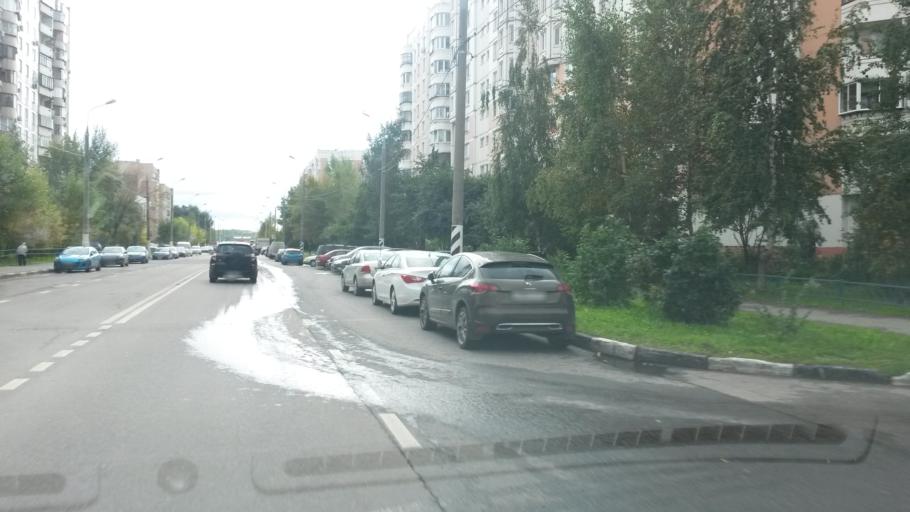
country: RU
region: Moskovskaya
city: Kommunarka
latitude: 55.5331
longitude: 37.5174
